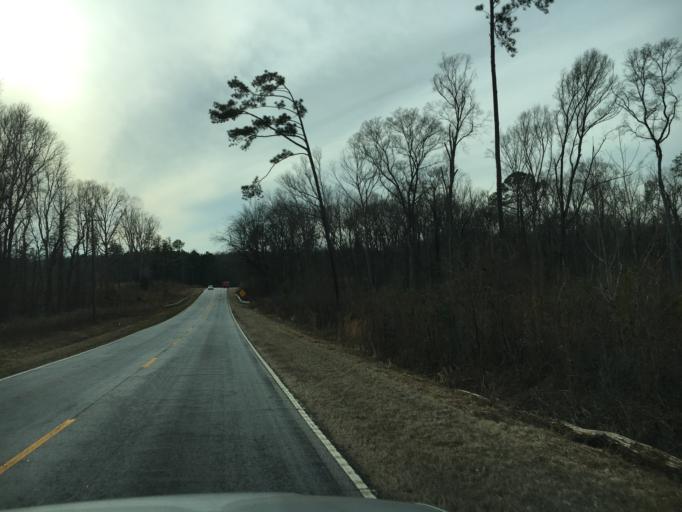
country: US
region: South Carolina
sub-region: Laurens County
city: Clinton
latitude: 34.5018
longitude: -81.8198
